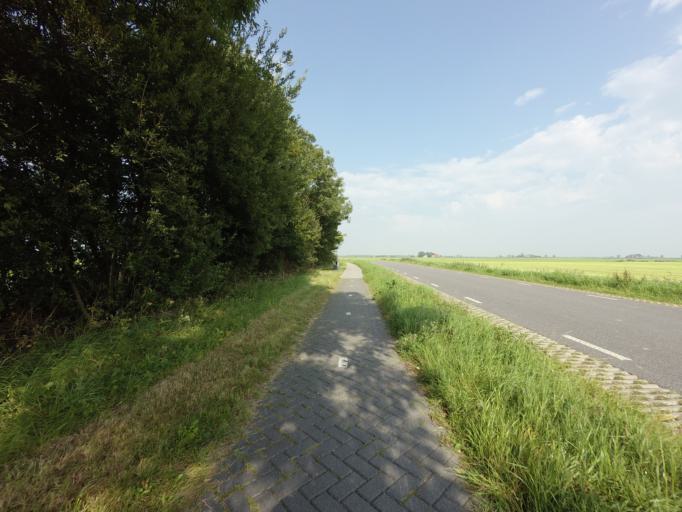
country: NL
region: Friesland
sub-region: Sudwest Fryslan
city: Bolsward
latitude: 53.0328
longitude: 5.5432
